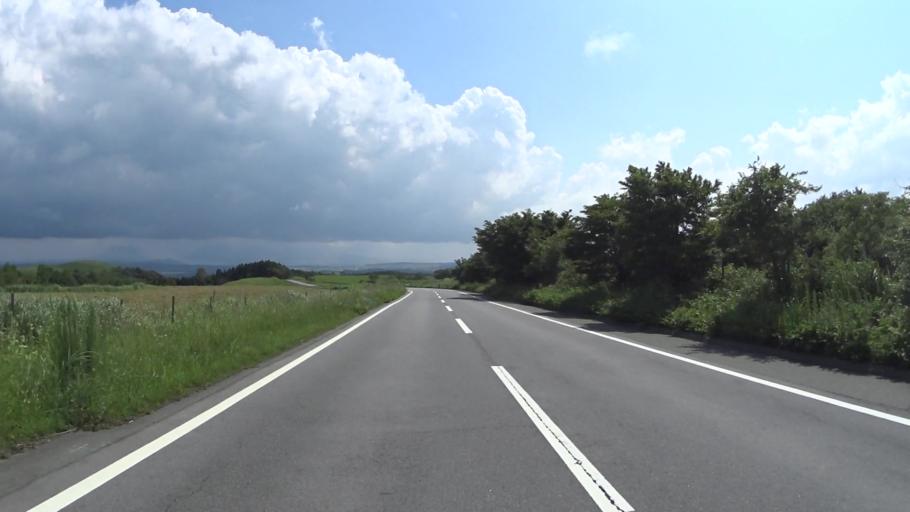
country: JP
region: Kumamoto
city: Aso
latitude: 33.0682
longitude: 131.1868
